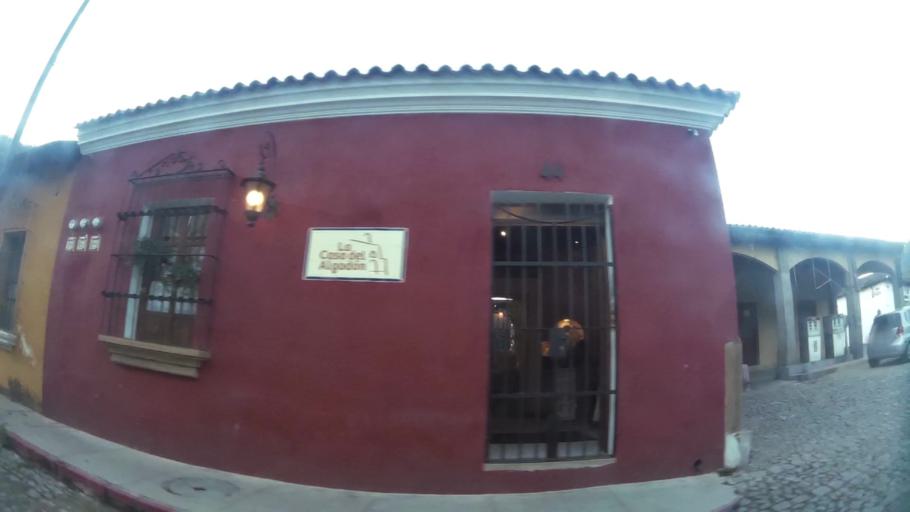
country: GT
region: Sacatepequez
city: Antigua Guatemala
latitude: 14.5575
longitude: -90.7278
